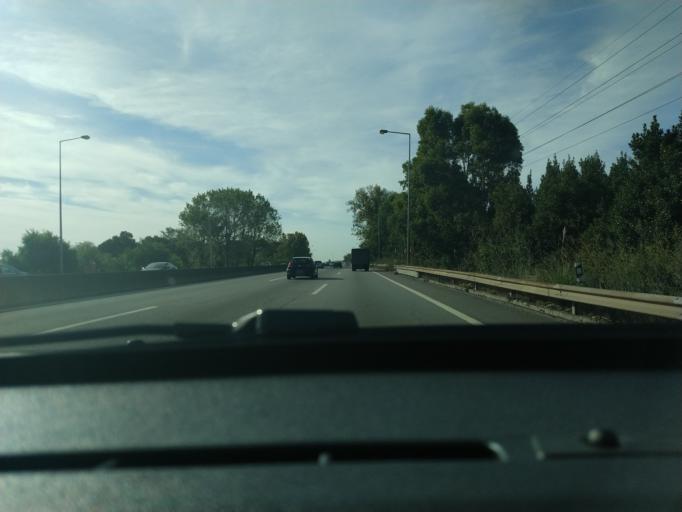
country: PT
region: Porto
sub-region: Vila Nova de Gaia
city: Canidelo
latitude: 41.1252
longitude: -8.6360
